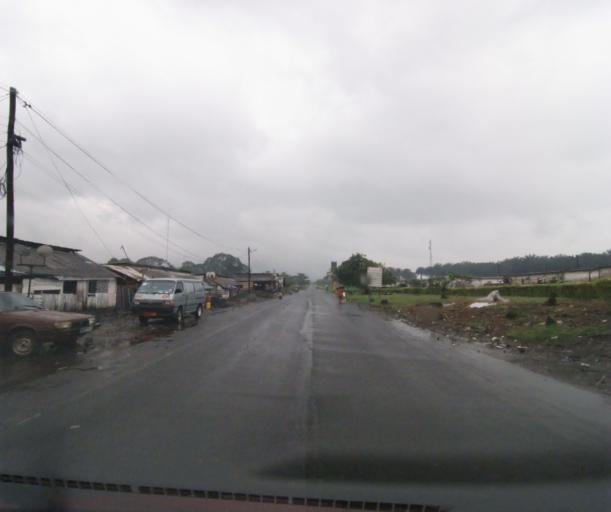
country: CM
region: South-West Province
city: Idenao
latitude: 4.2156
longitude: 8.9881
